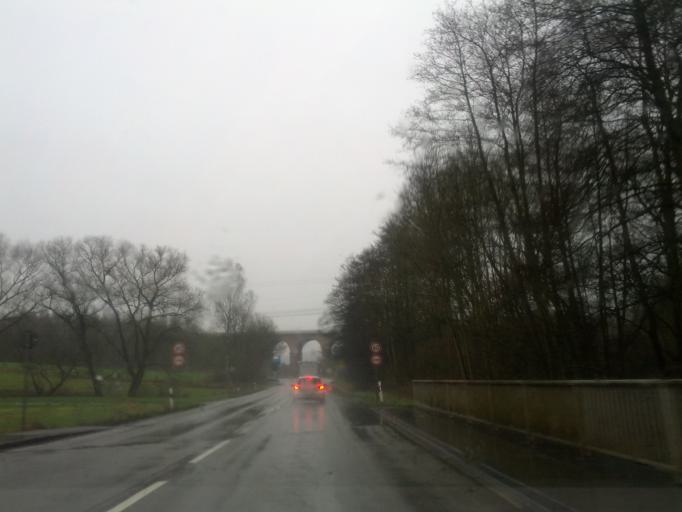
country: DE
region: Thuringia
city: Lauchroden
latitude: 51.0201
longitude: 10.1157
